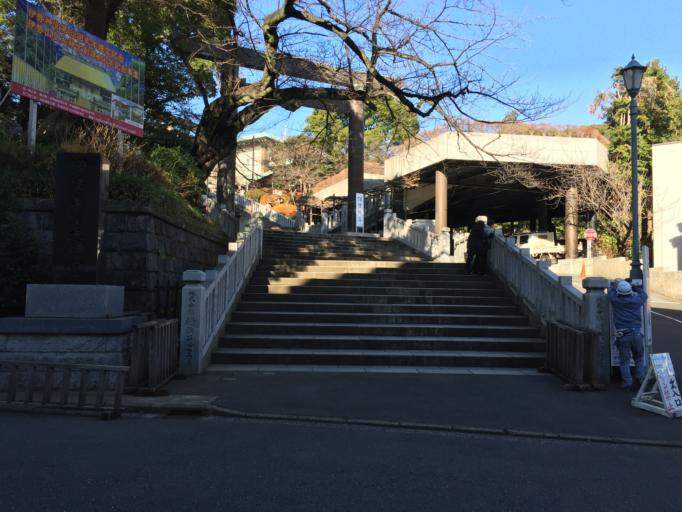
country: JP
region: Kanagawa
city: Yokohama
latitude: 35.4499
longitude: 139.6270
